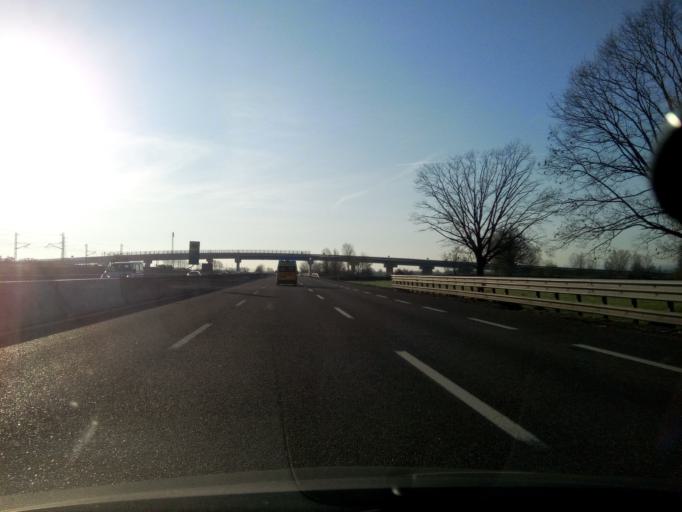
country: IT
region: Emilia-Romagna
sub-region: Provincia di Piacenza
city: Alseno
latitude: 44.9313
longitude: 9.9765
